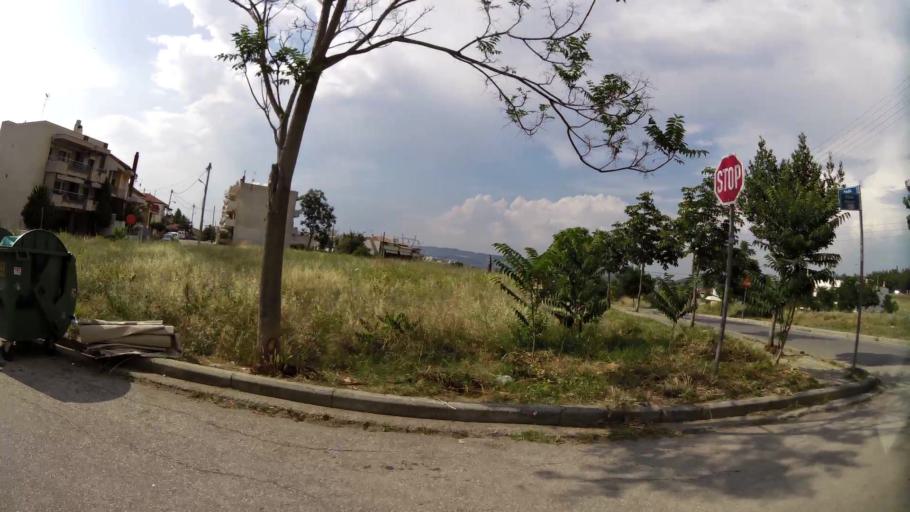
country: GR
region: Central Macedonia
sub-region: Nomos Thessalonikis
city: Polichni
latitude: 40.6640
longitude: 22.9521
